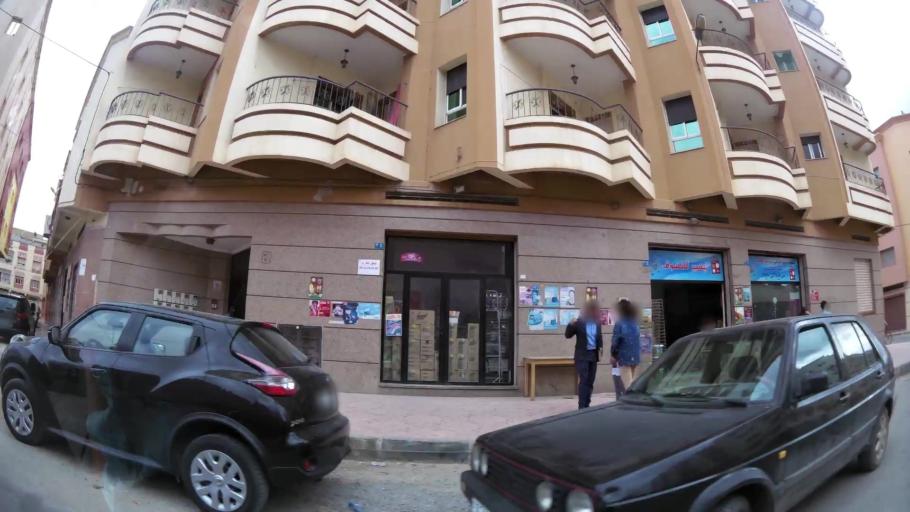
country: MA
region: Oriental
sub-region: Nador
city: Nador
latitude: 35.1674
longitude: -2.9351
